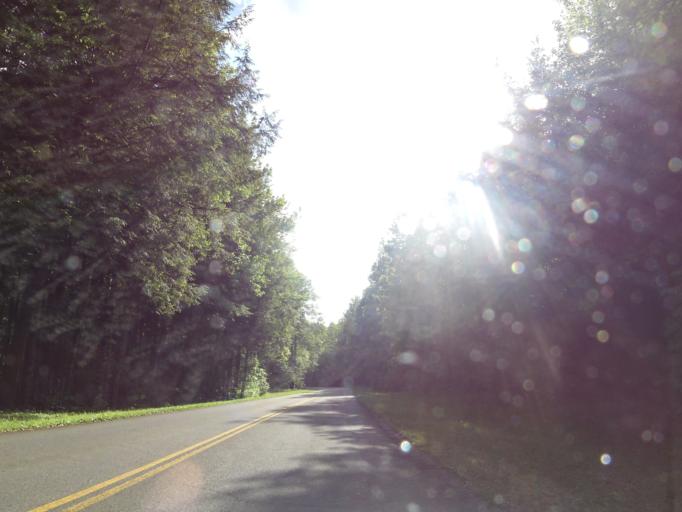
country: US
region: Tennessee
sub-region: Sevier County
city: Gatlinburg
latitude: 35.6824
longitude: -83.5474
